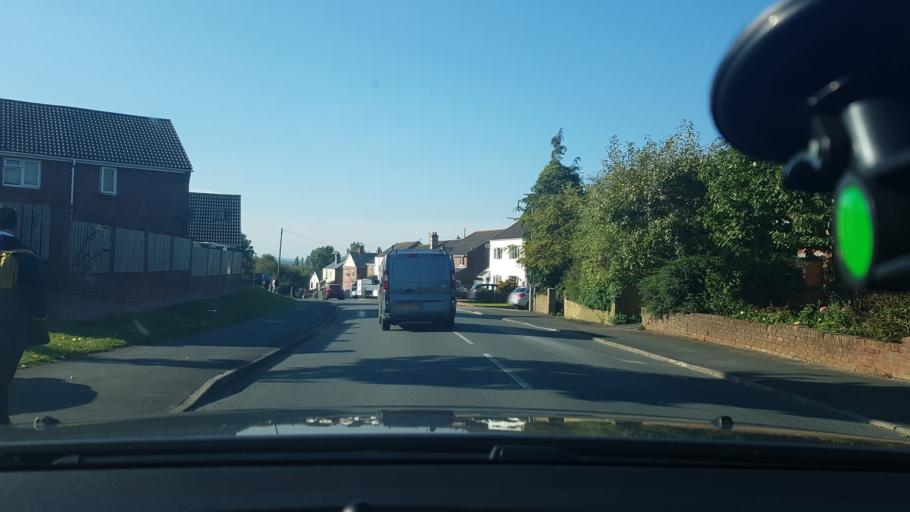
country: GB
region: England
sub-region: Gloucestershire
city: Gloucester
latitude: 51.8336
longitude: -2.2484
